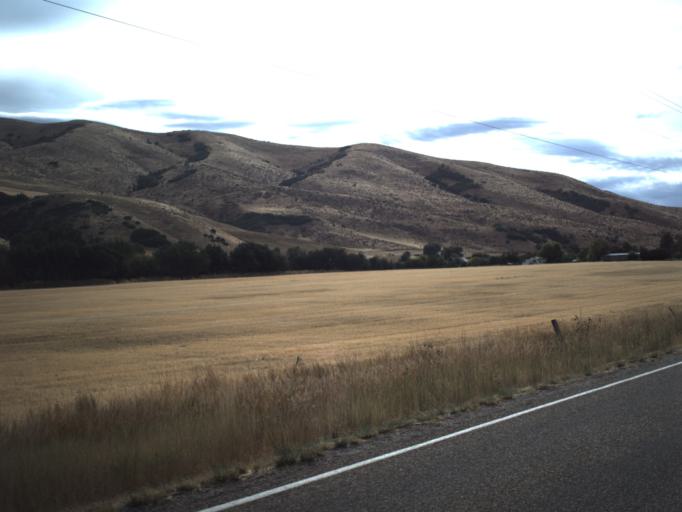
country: US
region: Utah
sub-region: Morgan County
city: Morgan
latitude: 40.9636
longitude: -111.6706
